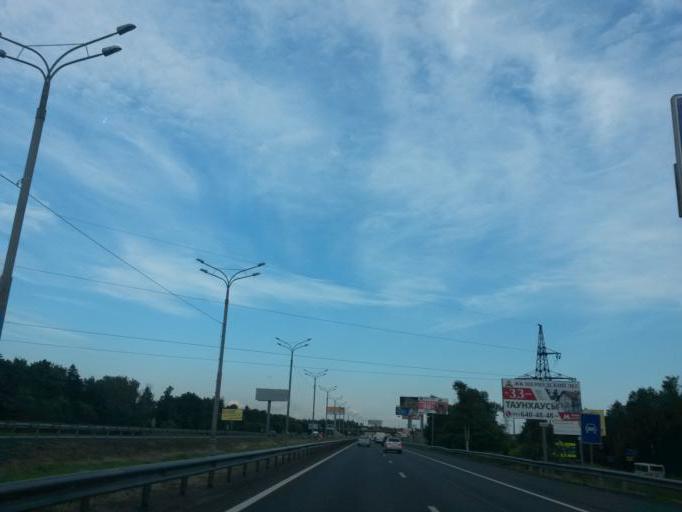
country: RU
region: Moskovskaya
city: Razvilka
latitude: 55.5803
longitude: 37.7511
